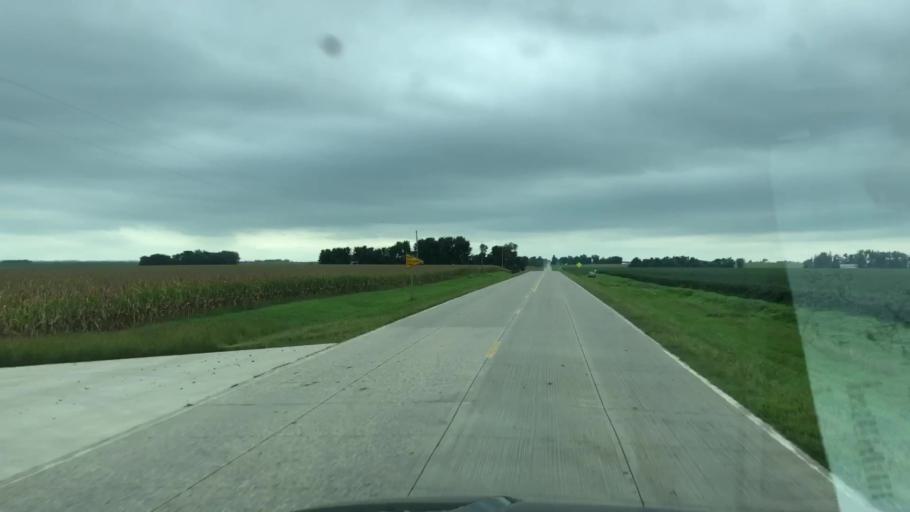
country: US
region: Iowa
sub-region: O'Brien County
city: Sheldon
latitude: 43.1241
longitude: -95.9790
